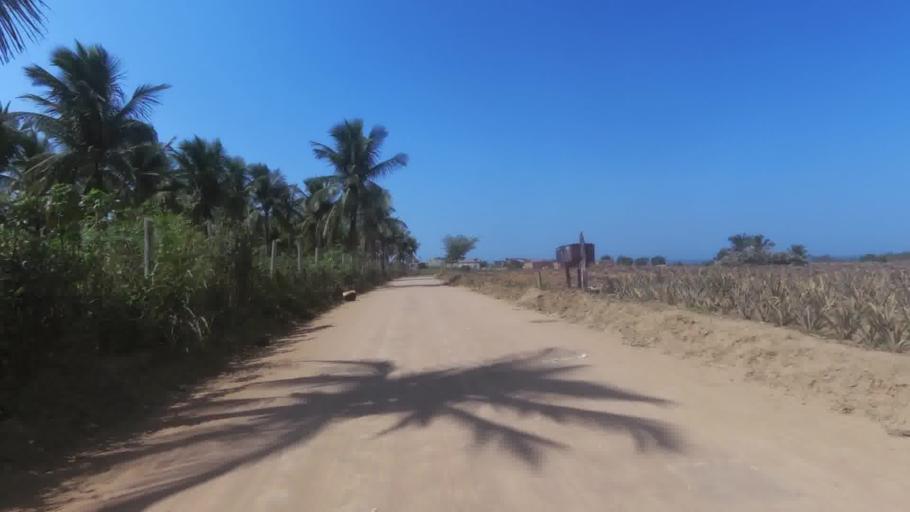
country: BR
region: Espirito Santo
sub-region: Marataizes
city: Marataizes
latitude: -21.1082
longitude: -40.8590
